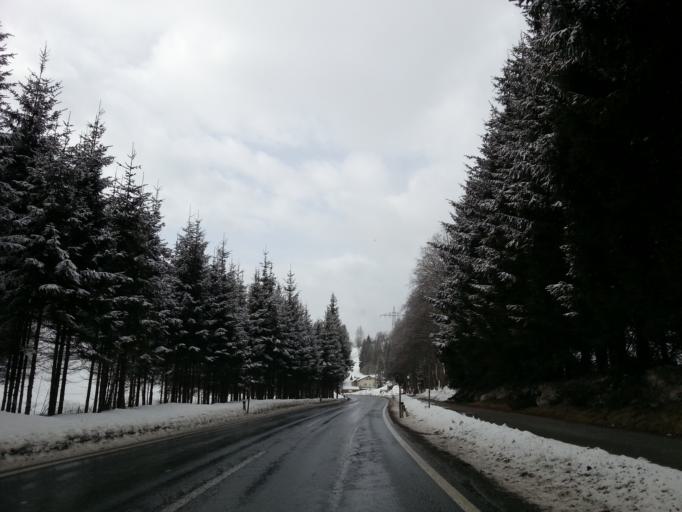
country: AT
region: Salzburg
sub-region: Politischer Bezirk Sankt Johann im Pongau
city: Eben im Pongau
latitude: 47.4503
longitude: 13.3666
